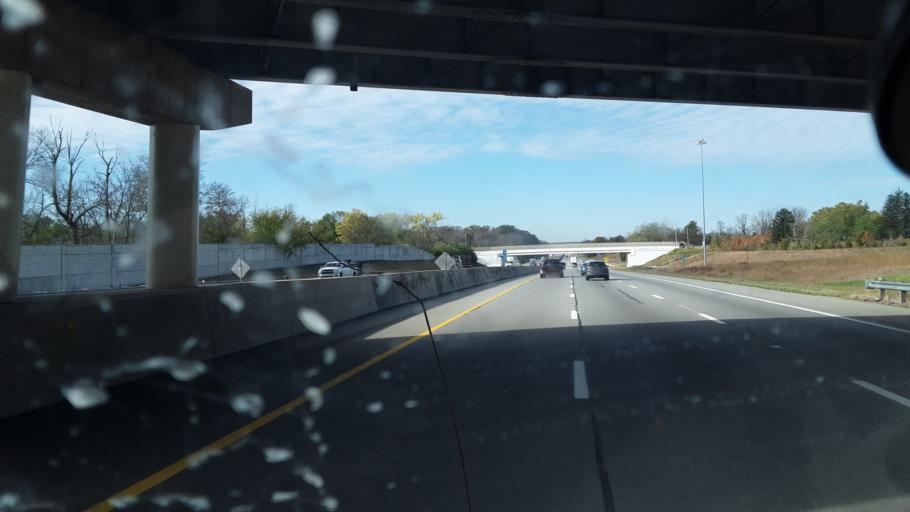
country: US
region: Ohio
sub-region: Montgomery County
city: Vandalia
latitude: 39.8647
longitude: -84.2228
